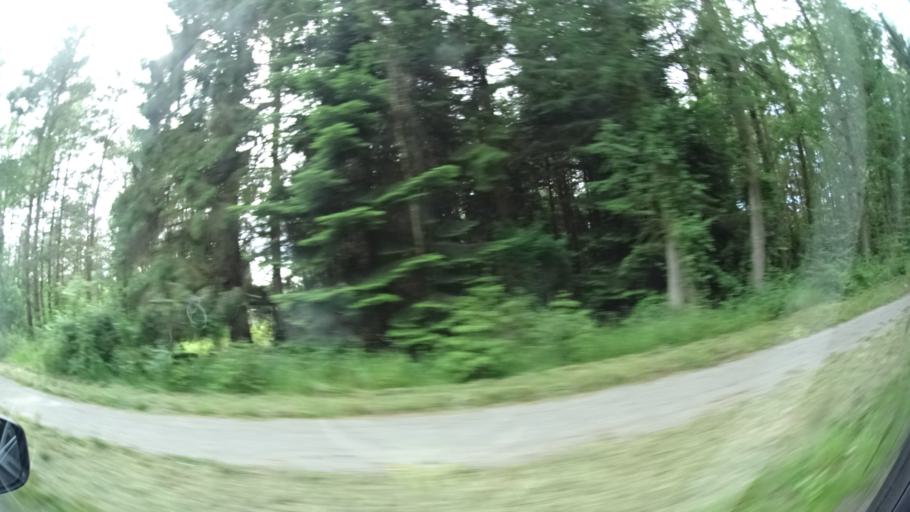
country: DK
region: Central Jutland
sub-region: Norddjurs Kommune
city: Grenaa
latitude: 56.4859
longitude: 10.7323
